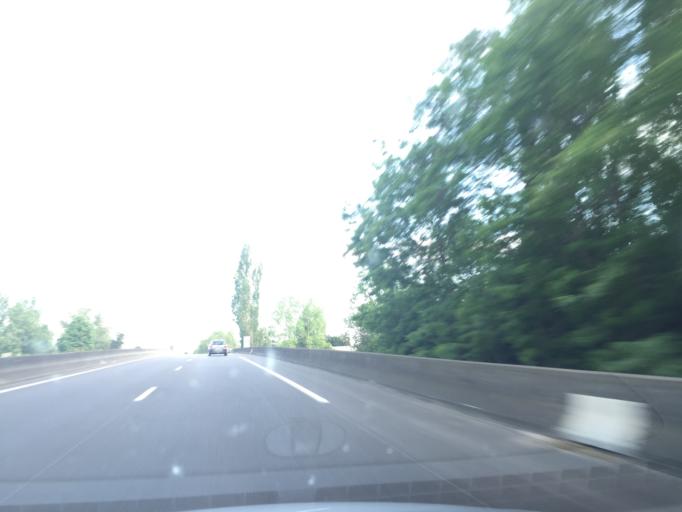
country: FR
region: Auvergne
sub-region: Departement du Puy-de-Dome
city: Riom
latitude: 45.8994
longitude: 3.1355
